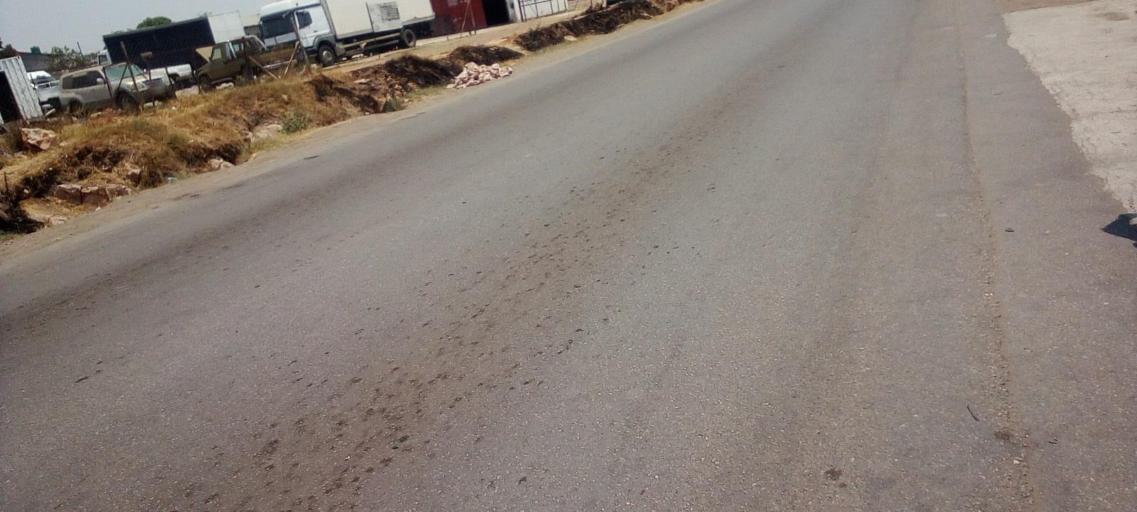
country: ZM
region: Lusaka
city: Lusaka
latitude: -15.4452
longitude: 28.2473
